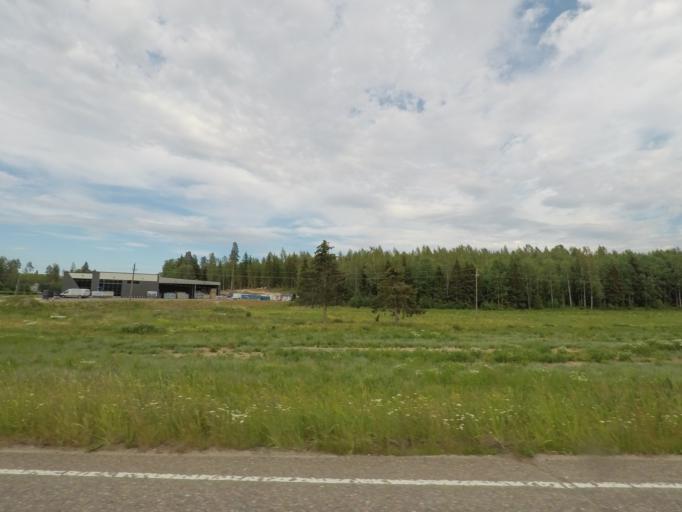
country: FI
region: Paijanne Tavastia
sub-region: Lahti
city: Hollola
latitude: 60.8640
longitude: 25.5012
